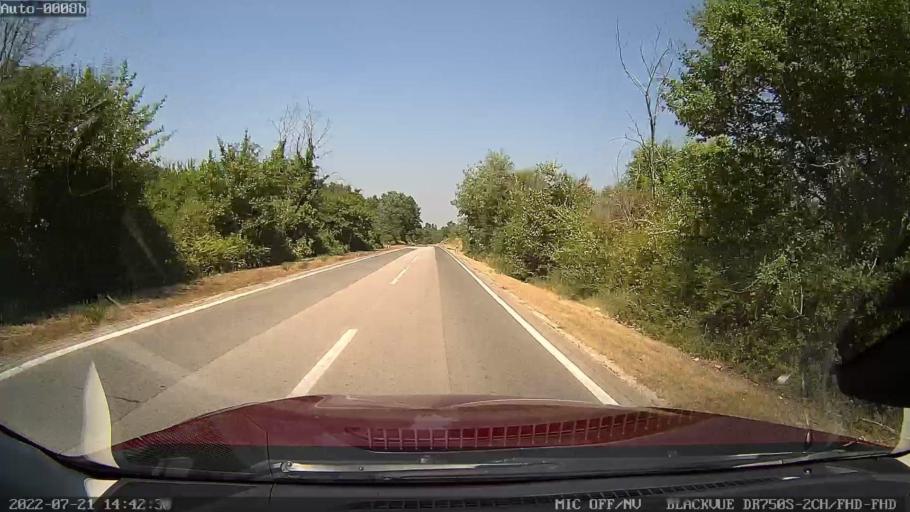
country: HR
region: Istarska
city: Vodnjan
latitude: 45.0989
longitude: 13.8826
